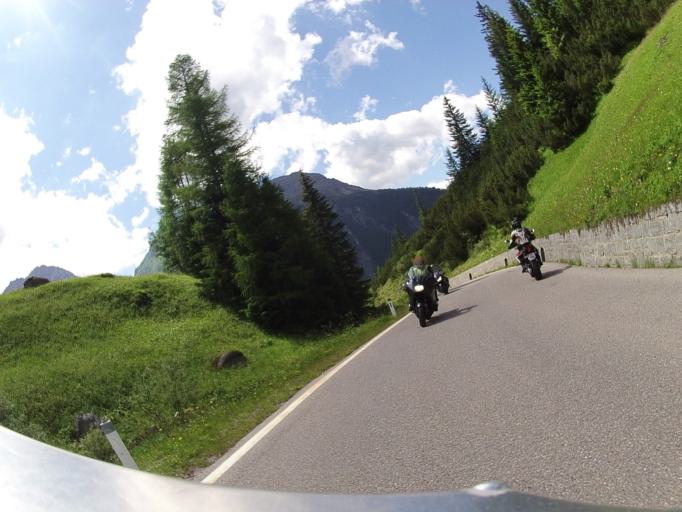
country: AT
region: Tyrol
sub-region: Politischer Bezirk Reutte
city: Namlos
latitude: 47.2833
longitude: 10.6195
